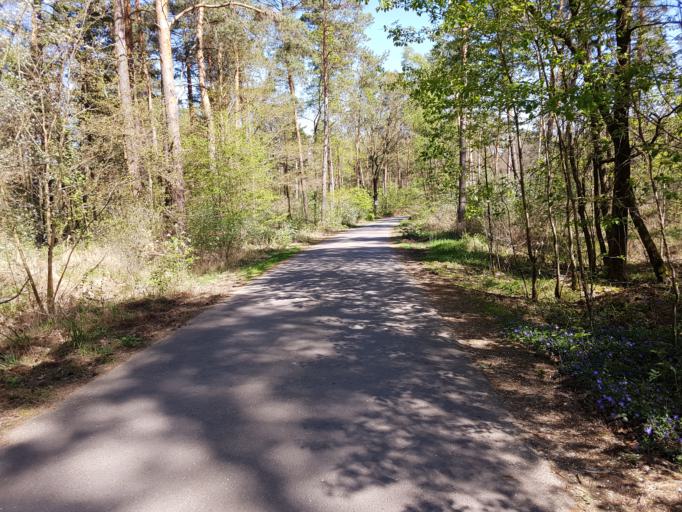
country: DE
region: Brandenburg
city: Groden
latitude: 51.3952
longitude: 13.5608
